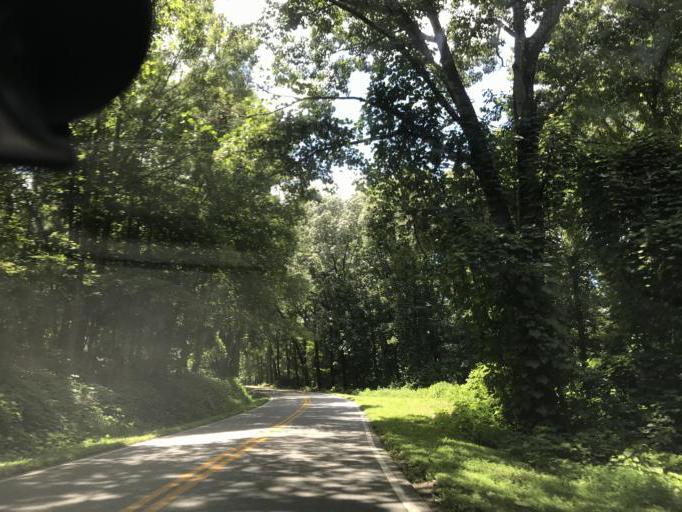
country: US
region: Georgia
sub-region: Fulton County
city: Milton
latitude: 34.2103
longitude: -84.2581
